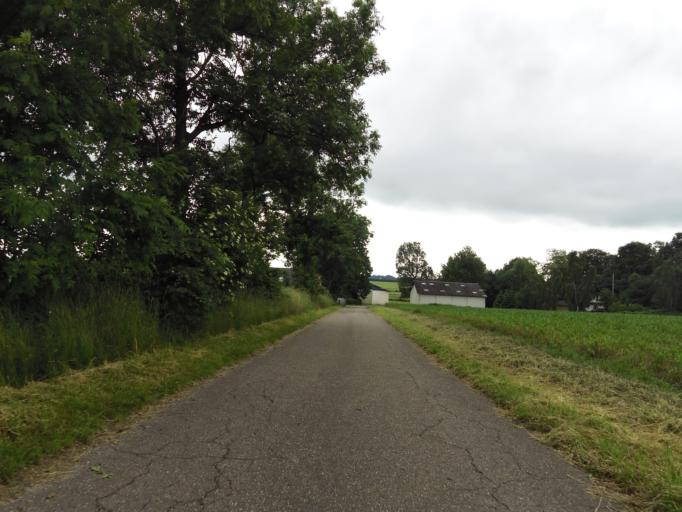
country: DK
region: South Denmark
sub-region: Tonder Kommune
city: Toftlund
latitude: 55.1022
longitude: 9.0916
